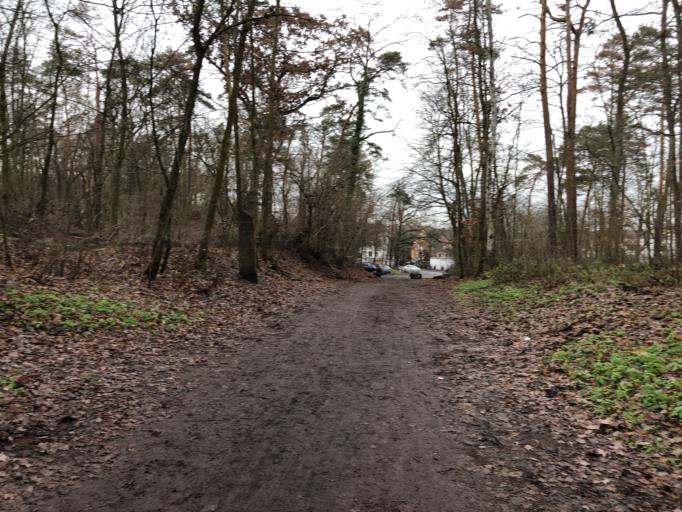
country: DE
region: Saxony-Anhalt
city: Halle Neustadt
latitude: 51.5092
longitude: 11.9051
